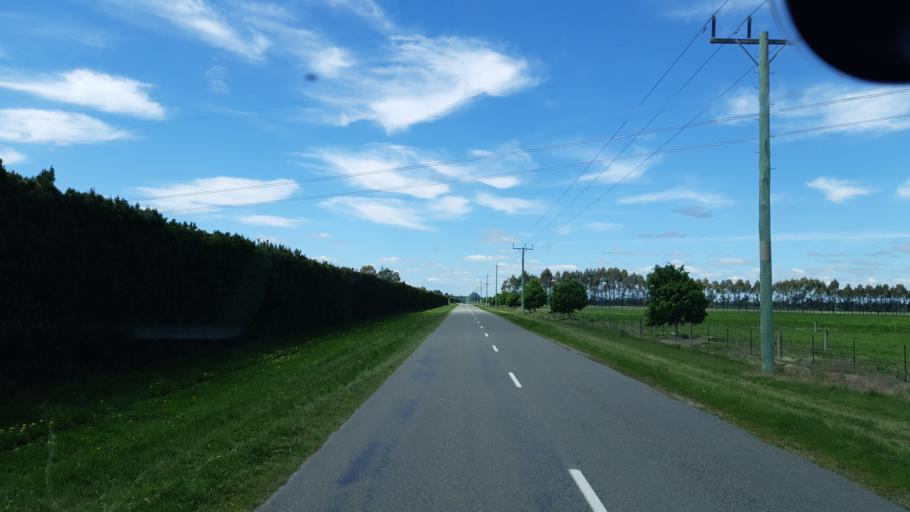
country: NZ
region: Canterbury
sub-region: Ashburton District
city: Methven
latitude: -43.7240
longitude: 171.4852
